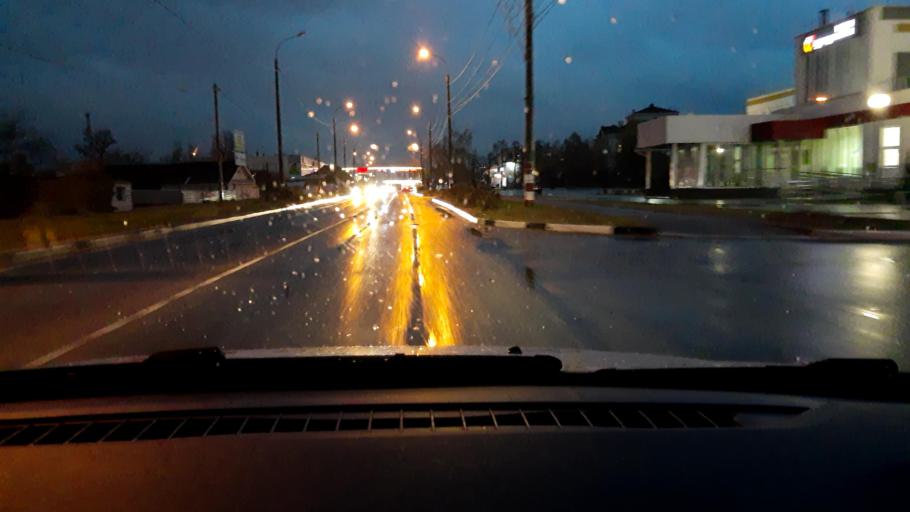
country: RU
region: Nizjnij Novgorod
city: Bor
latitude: 56.3615
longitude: 44.0490
